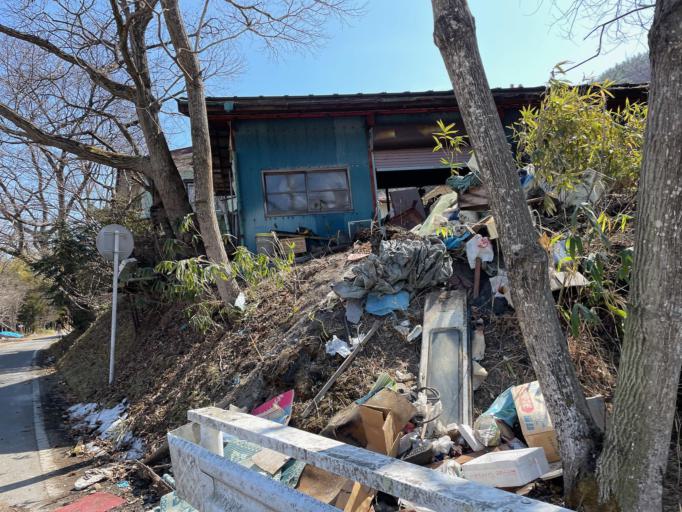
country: JP
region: Gunma
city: Nakanojomachi
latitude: 36.5707
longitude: 138.6288
